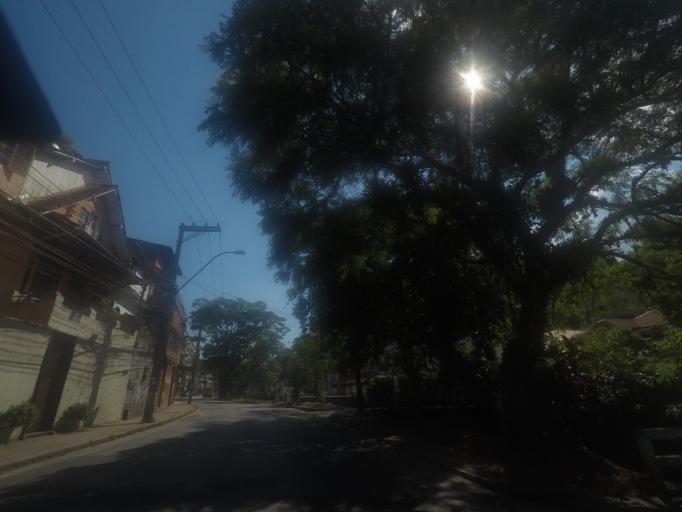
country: BR
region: Rio de Janeiro
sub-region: Petropolis
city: Petropolis
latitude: -22.5194
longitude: -43.1875
